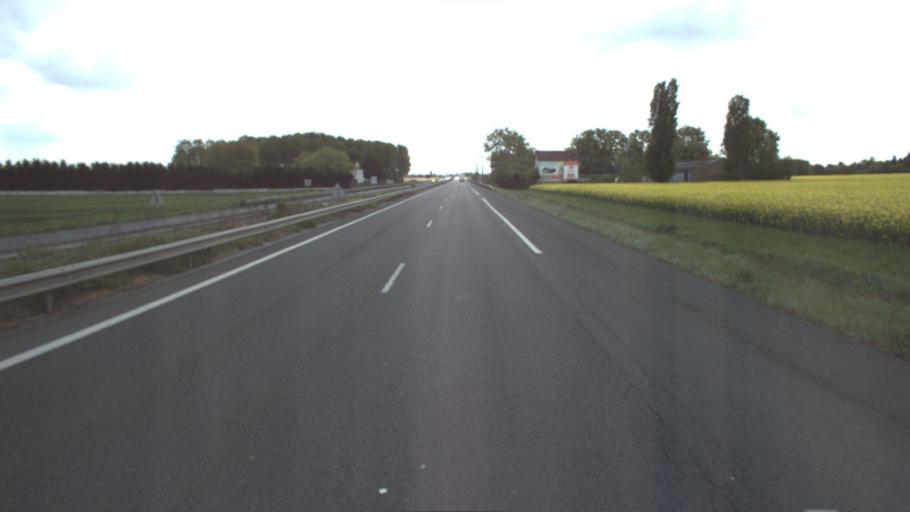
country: FR
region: Ile-de-France
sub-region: Departement de Seine-et-Marne
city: Rozay-en-Brie
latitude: 48.6902
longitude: 2.9208
